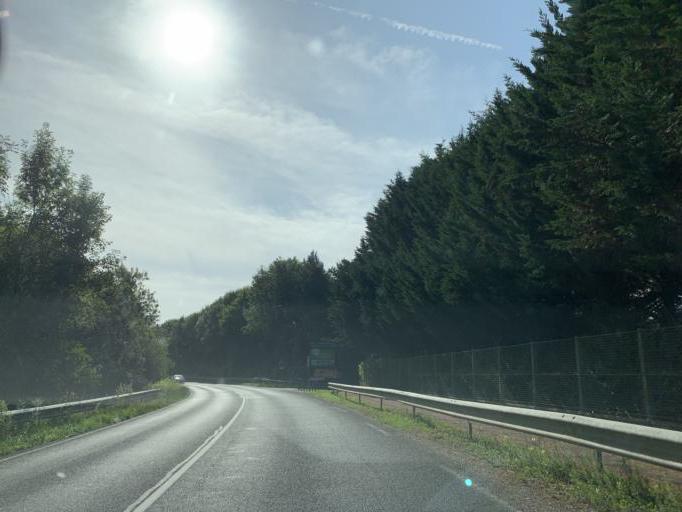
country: FR
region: Ile-de-France
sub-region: Departement de Seine-et-Marne
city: Annet-sur-Marne
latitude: 48.9204
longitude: 2.7260
